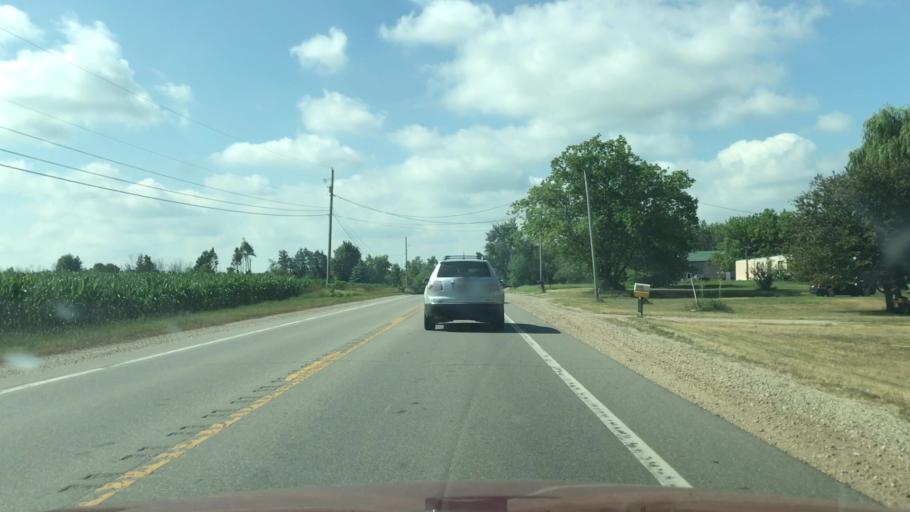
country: US
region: Michigan
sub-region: Kent County
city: Kent City
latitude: 43.3035
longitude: -85.8106
